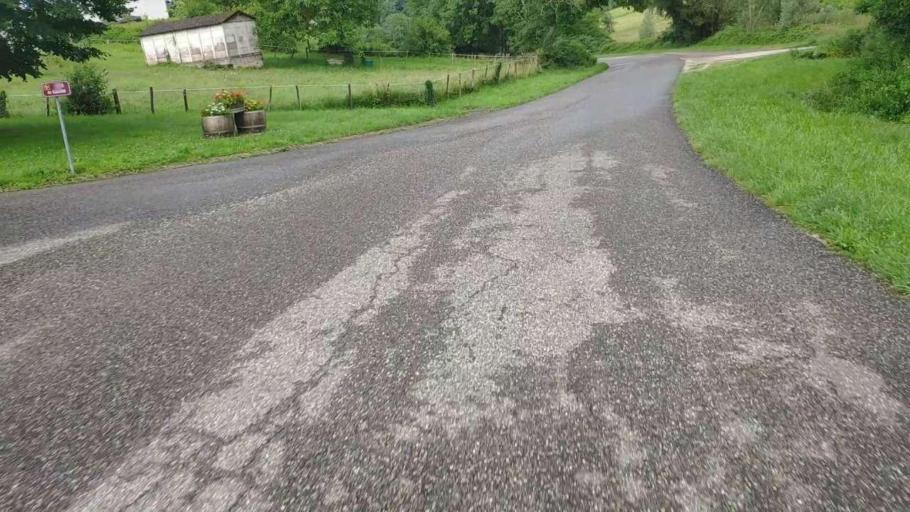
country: FR
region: Franche-Comte
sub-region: Departement du Jura
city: Poligny
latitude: 46.8031
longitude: 5.6199
